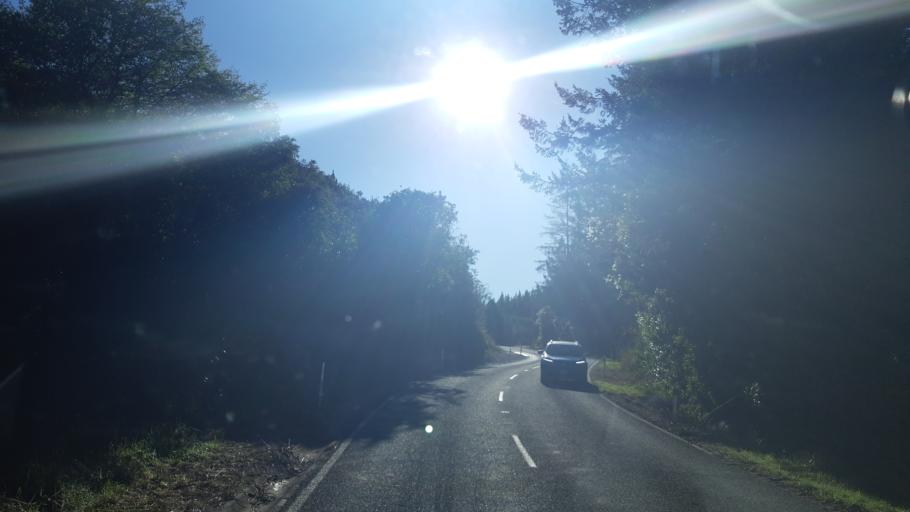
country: NZ
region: Tasman
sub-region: Tasman District
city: Motueka
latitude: -41.0456
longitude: 172.9783
